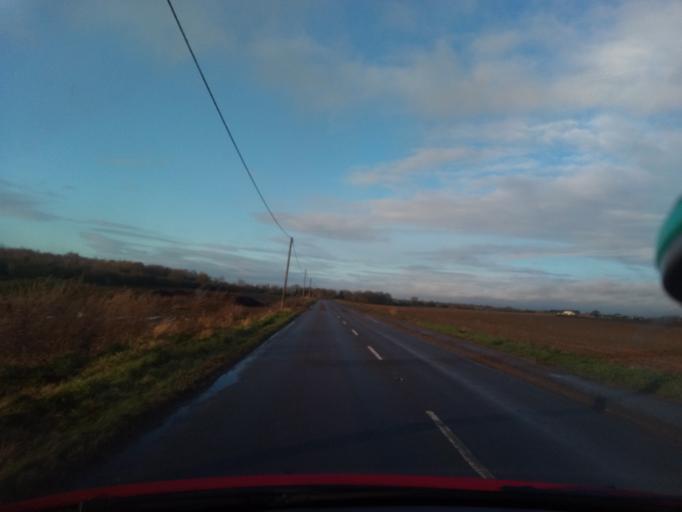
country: GB
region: England
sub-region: Derbyshire
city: Melbourne
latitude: 52.8498
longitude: -1.4179
